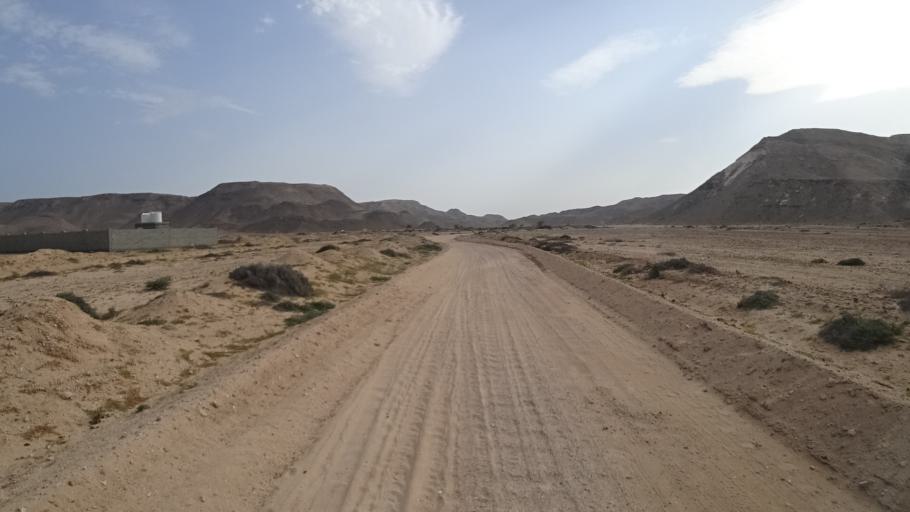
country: OM
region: Ash Sharqiyah
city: Sur
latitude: 22.4388
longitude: 59.8197
